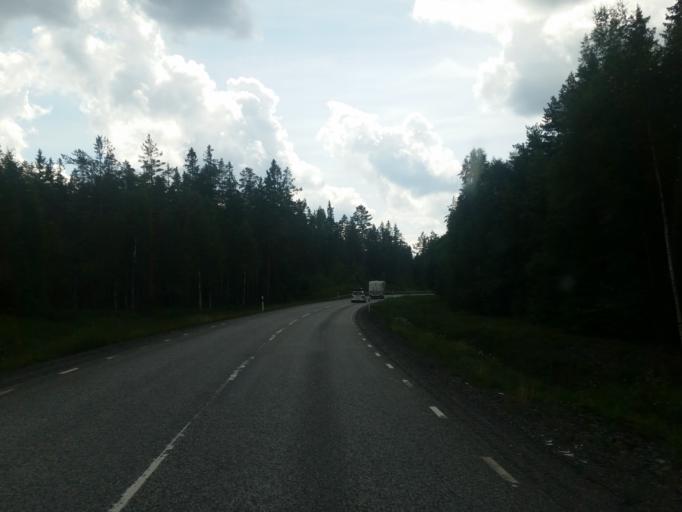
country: SE
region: OErebro
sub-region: Ljusnarsbergs Kommun
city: Kopparberg
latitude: 59.9395
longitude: 15.0260
